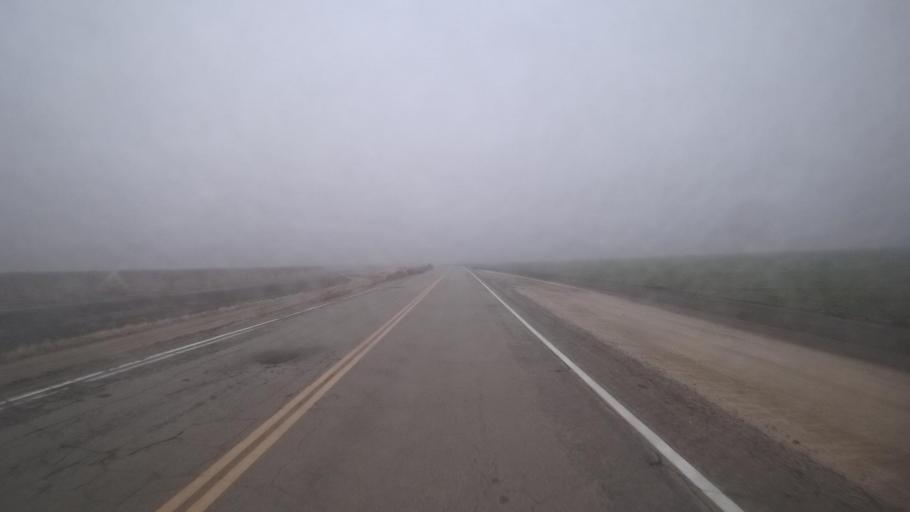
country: US
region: California
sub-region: Kern County
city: Buttonwillow
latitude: 35.4369
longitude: -119.5468
